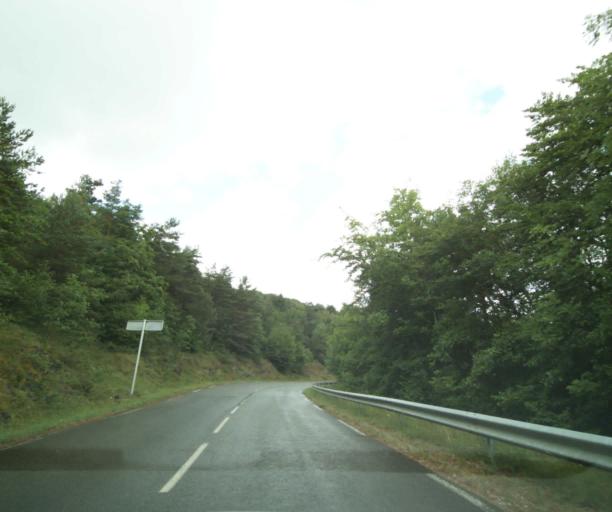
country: FR
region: Languedoc-Roussillon
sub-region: Departement de la Lozere
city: La Canourgue
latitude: 44.3997
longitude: 3.1414
